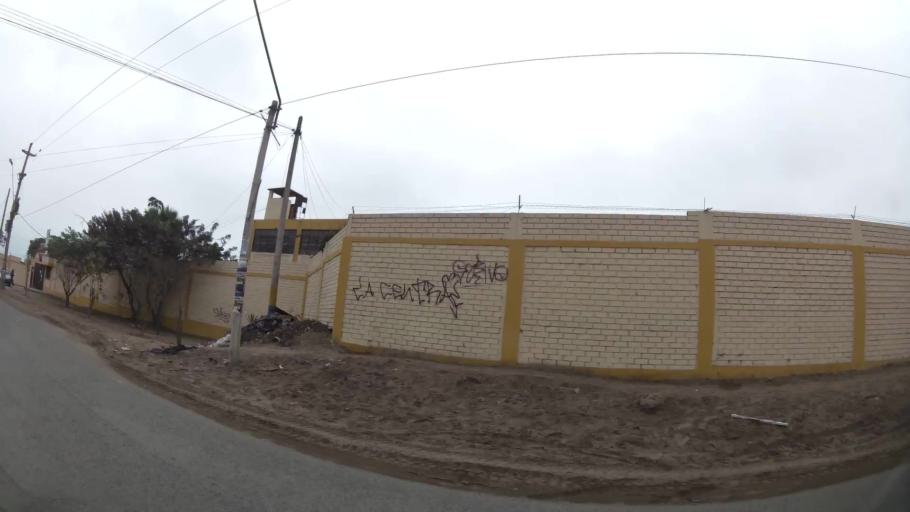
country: PE
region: Lima
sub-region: Lima
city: Surco
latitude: -12.2162
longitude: -76.9301
